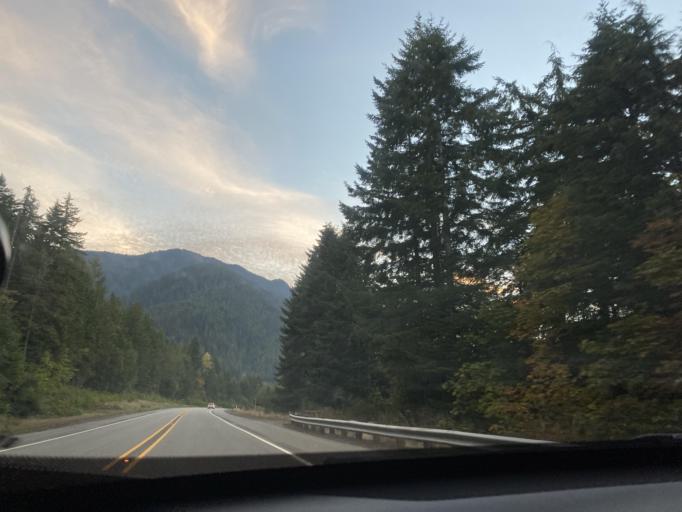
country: US
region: Washington
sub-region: Clallam County
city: Port Angeles
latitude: 48.0652
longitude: -123.5908
